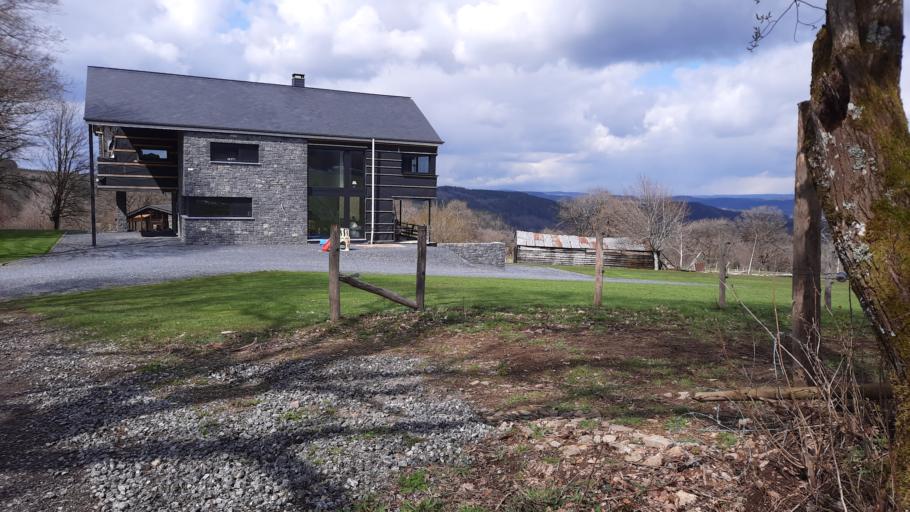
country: BE
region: Wallonia
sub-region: Province du Luxembourg
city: Manhay
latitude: 50.2792
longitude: 5.7198
